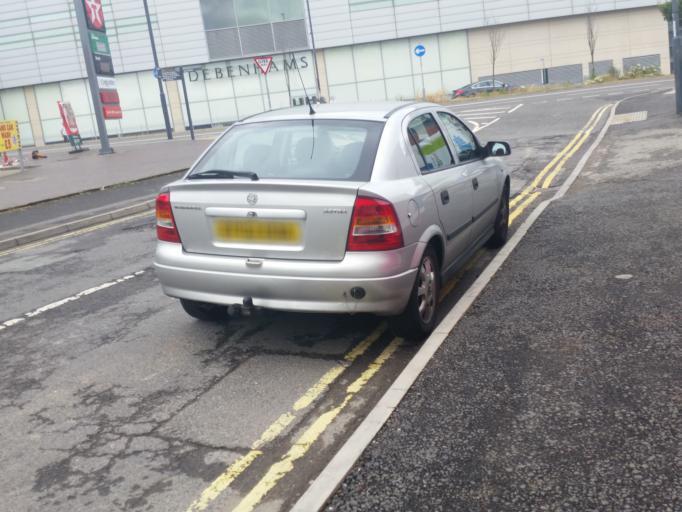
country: GB
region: England
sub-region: Derby
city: Derby
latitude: 52.9184
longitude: -1.4703
